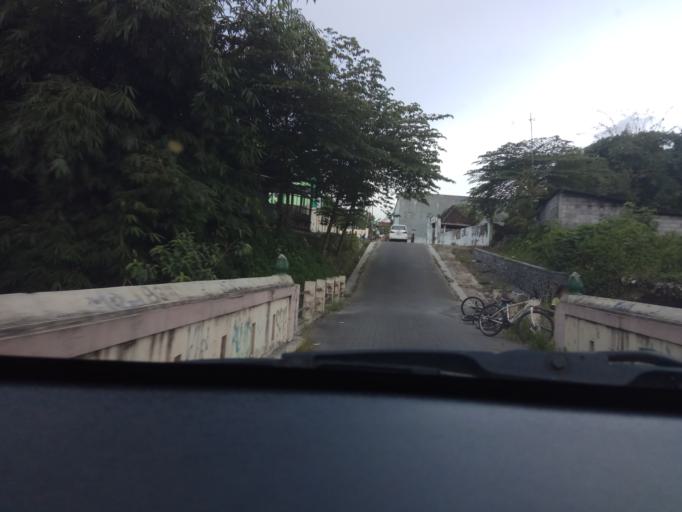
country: ID
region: Daerah Istimewa Yogyakarta
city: Depok
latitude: -7.7607
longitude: 110.4010
